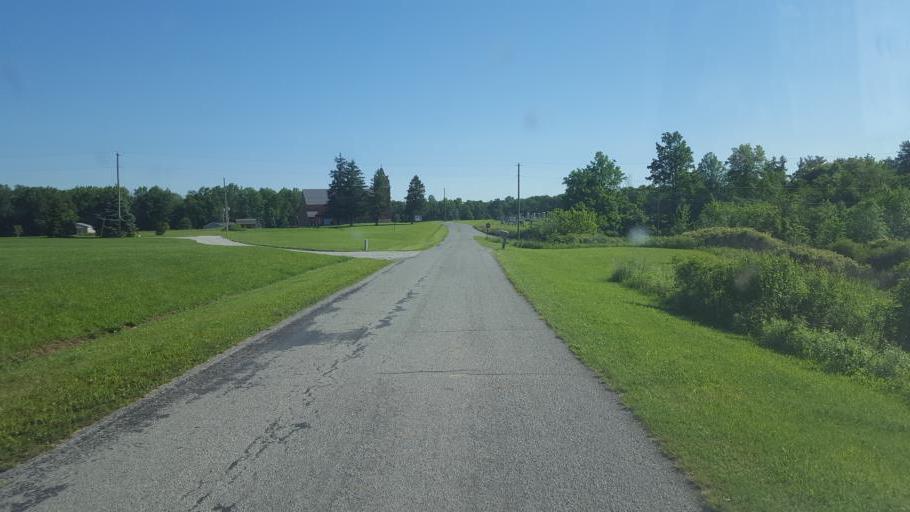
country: US
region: Ohio
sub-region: Crawford County
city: Bucyrus
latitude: 40.7422
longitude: -82.9159
